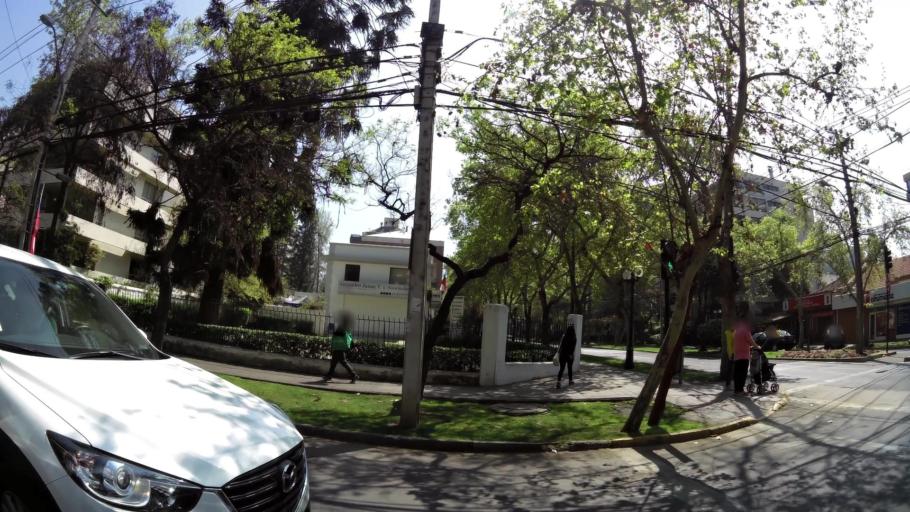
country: CL
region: Santiago Metropolitan
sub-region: Provincia de Santiago
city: Villa Presidente Frei, Nunoa, Santiago, Chile
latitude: -33.4219
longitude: -70.5986
